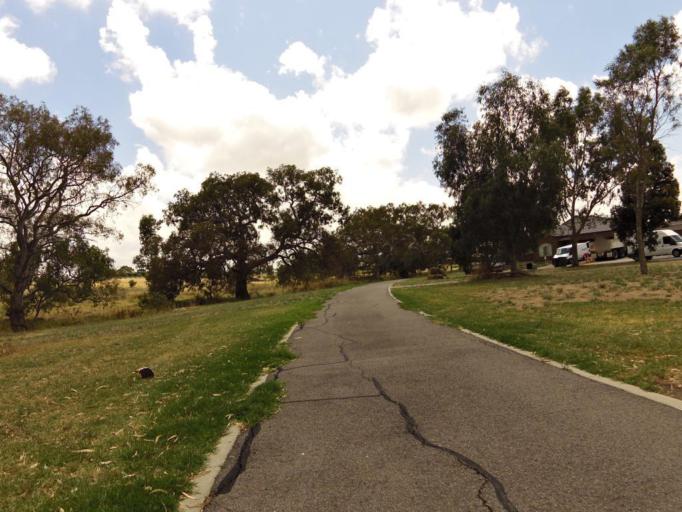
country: AU
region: Victoria
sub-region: Hume
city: Craigieburn
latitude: -37.5814
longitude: 144.9165
